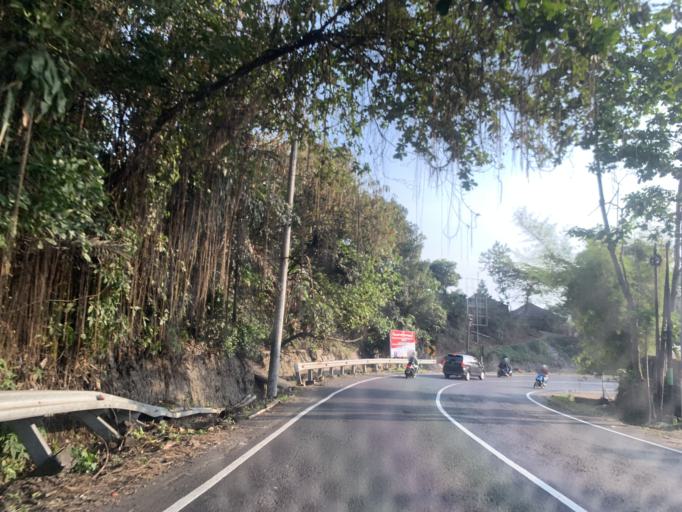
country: ID
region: Bali
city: Bajera
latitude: -8.5017
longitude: 115.0235
